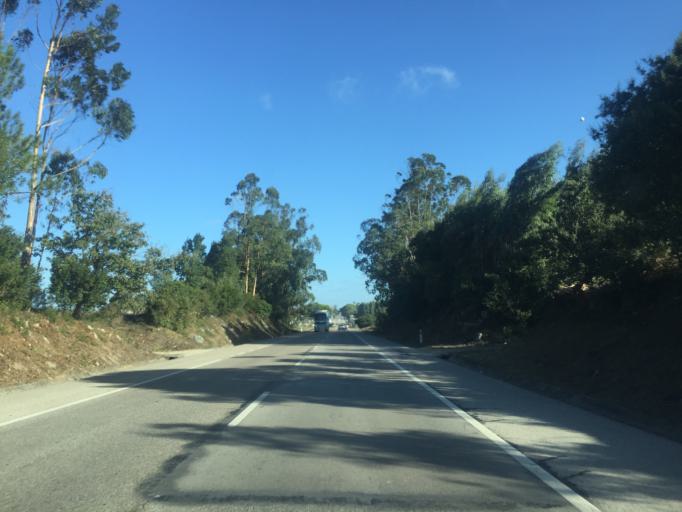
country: PT
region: Leiria
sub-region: Alcobaca
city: Turquel
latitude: 39.4580
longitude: -8.9465
